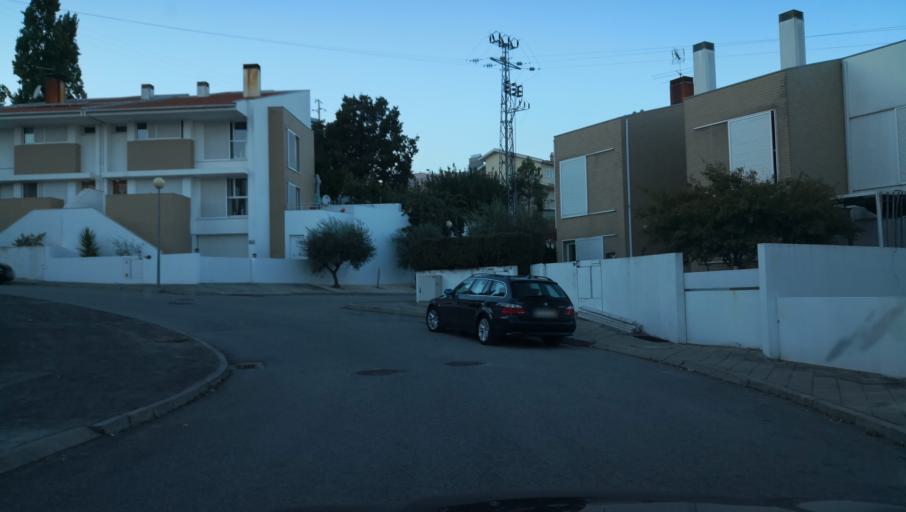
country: PT
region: Vila Real
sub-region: Vila Real
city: Vila Real
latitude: 41.3088
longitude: -7.7660
